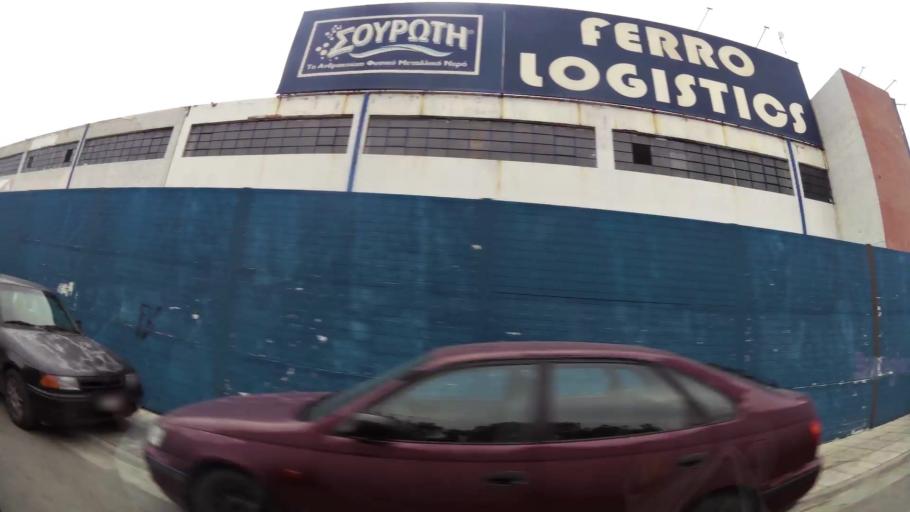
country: GR
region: Attica
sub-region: Nomos Piraios
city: Agios Ioannis Rentis
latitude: 37.9717
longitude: 23.6733
